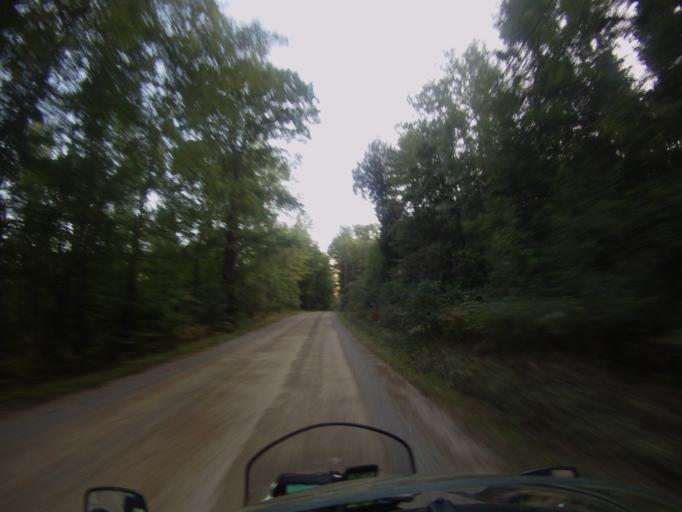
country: US
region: Vermont
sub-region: Addison County
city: Middlebury (village)
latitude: 43.9987
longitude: -73.0401
